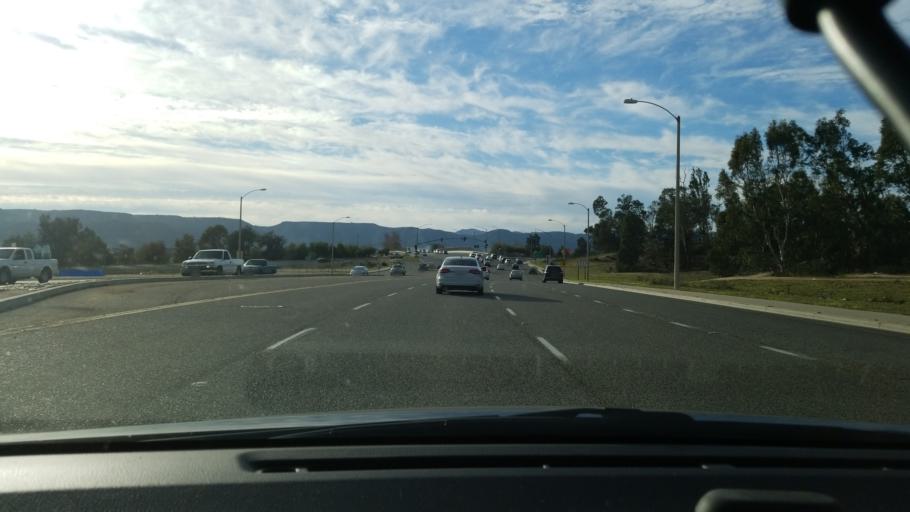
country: US
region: California
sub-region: Riverside County
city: Murrieta
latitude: 33.5552
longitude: -117.1881
